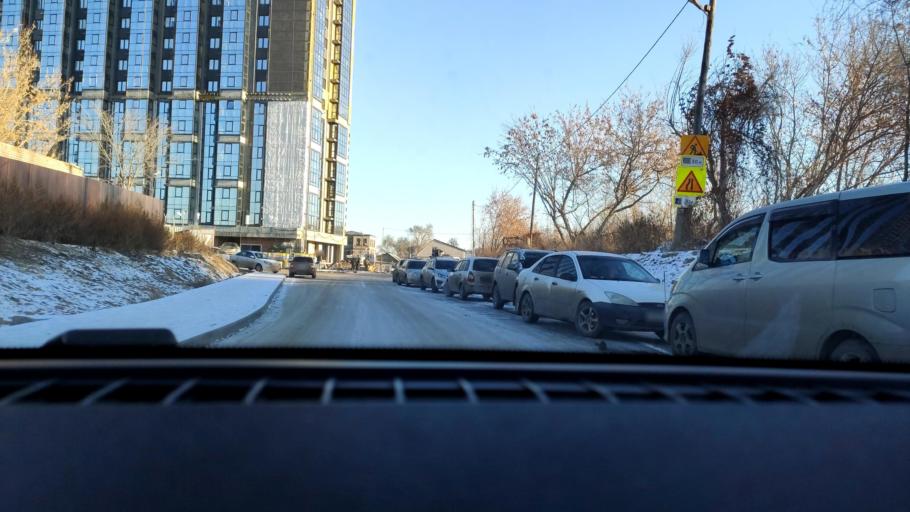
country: RU
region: Samara
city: Samara
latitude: 53.2174
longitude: 50.1374
